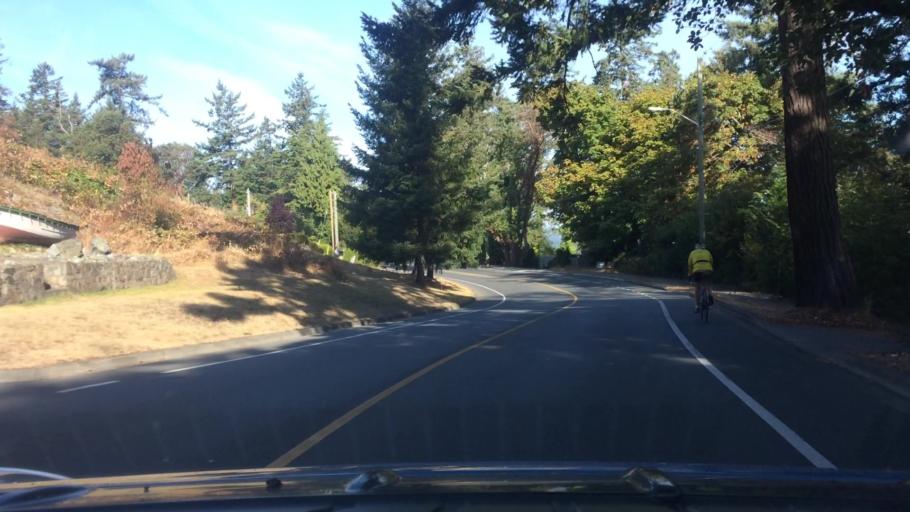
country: CA
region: British Columbia
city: Oak Bay
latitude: 48.5020
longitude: -123.3435
